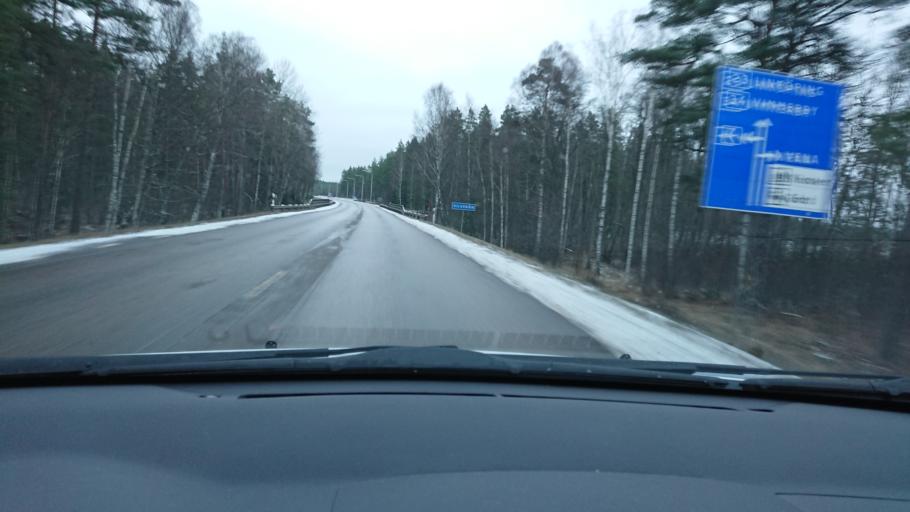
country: SE
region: Kalmar
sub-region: Hultsfreds Kommun
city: Hultsfred
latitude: 57.5142
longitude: 15.8404
